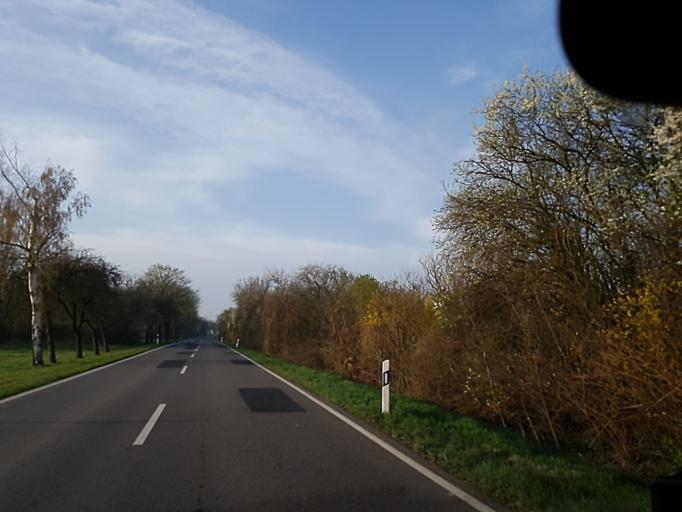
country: DE
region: Brandenburg
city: Muhlberg
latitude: 51.4455
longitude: 13.2687
